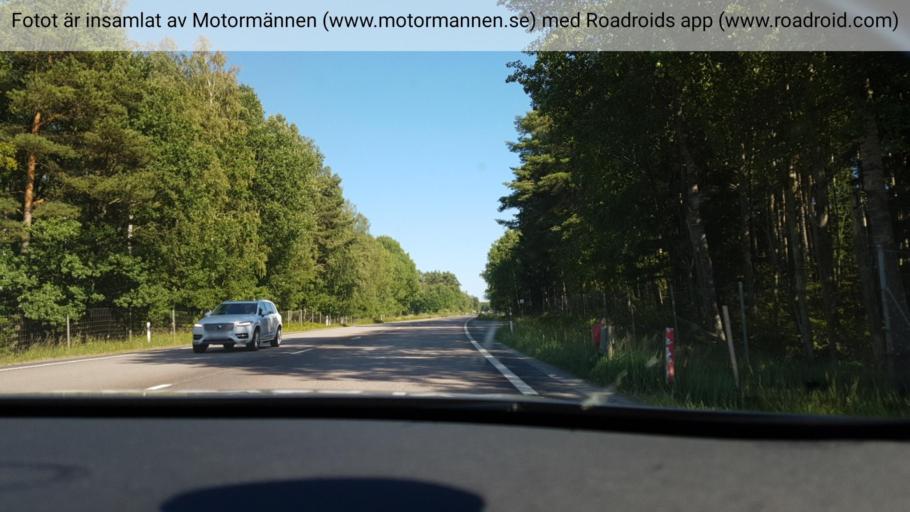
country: SE
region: Vaestra Goetaland
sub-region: Lidkopings Kommun
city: Vinninga
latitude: 58.4276
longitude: 13.3263
